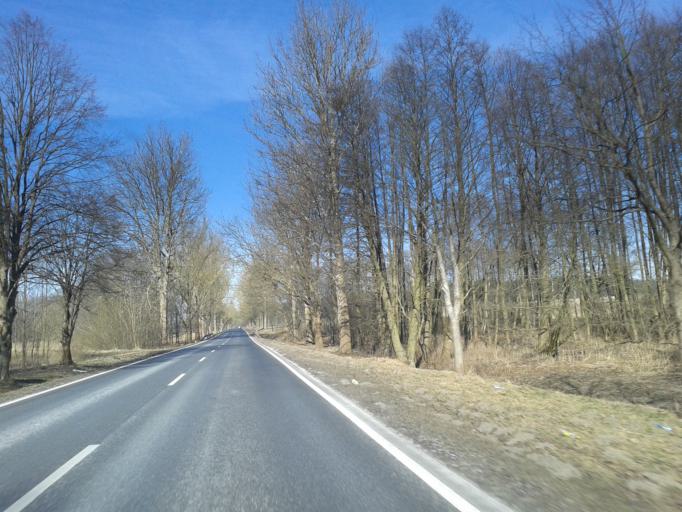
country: PL
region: Greater Poland Voivodeship
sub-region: Powiat zlotowski
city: Okonek
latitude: 53.4823
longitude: 16.8724
